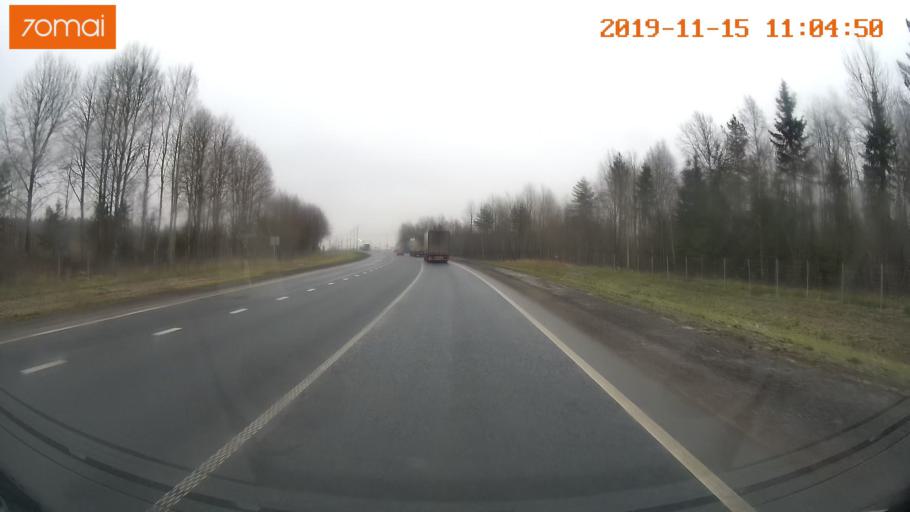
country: RU
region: Vologda
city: Chebsara
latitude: 59.1185
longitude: 38.9923
